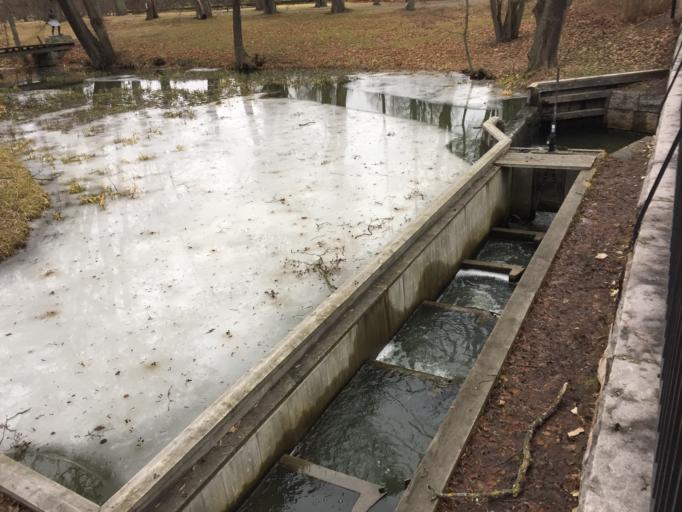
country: SE
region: Stockholm
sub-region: Norrtalje Kommun
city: Bergshamra
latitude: 59.3890
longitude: 18.0165
